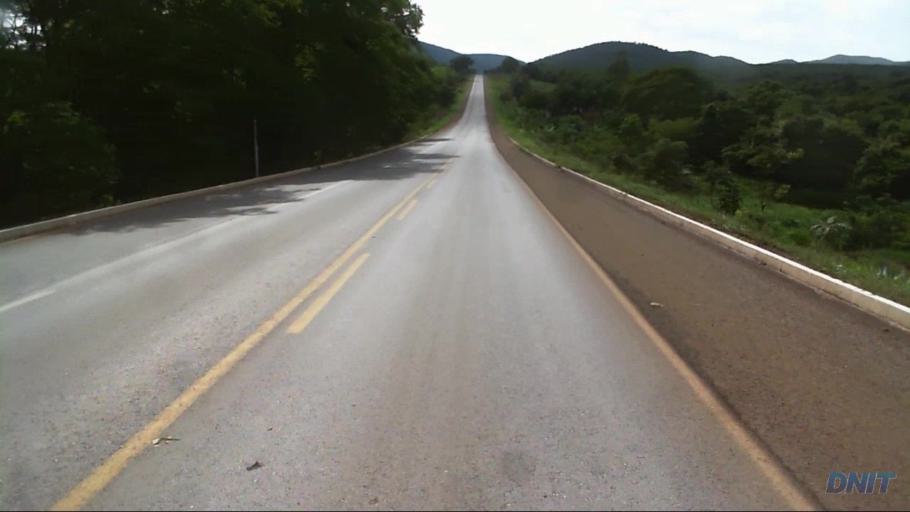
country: BR
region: Goias
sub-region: Barro Alto
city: Barro Alto
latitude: -14.8710
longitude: -49.0051
